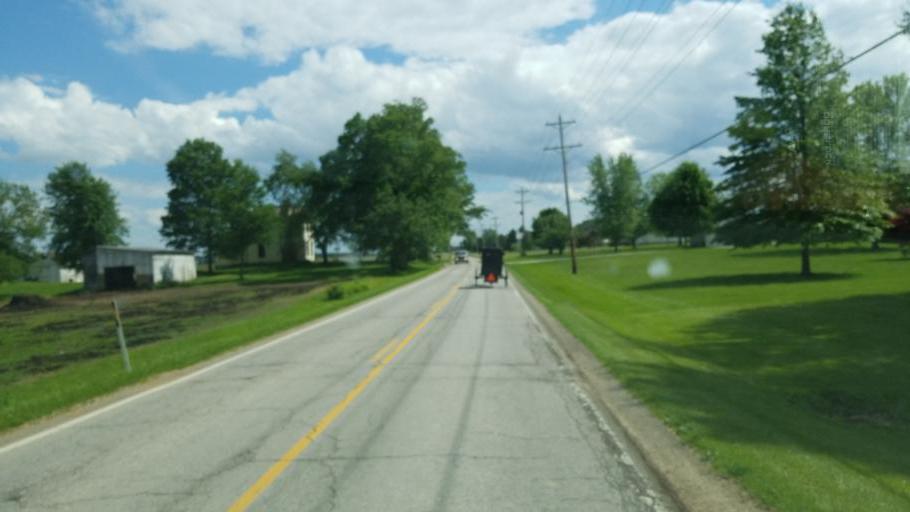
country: US
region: Ohio
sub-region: Huron County
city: Plymouth
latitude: 41.0441
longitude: -82.6090
